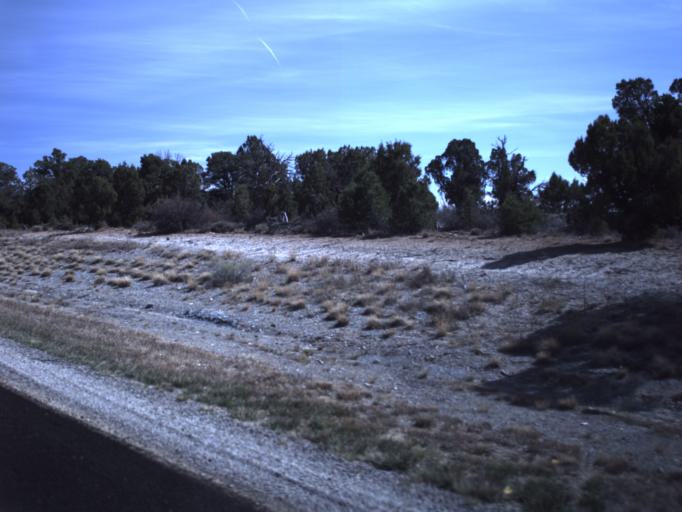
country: US
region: Colorado
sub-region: Dolores County
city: Dove Creek
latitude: 37.8244
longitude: -109.0696
